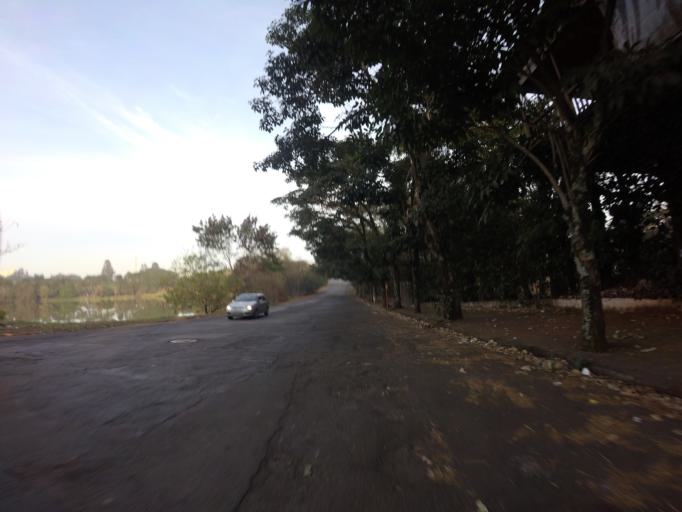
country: BR
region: Sao Paulo
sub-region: Piracicaba
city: Piracicaba
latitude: -22.7333
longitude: -47.5915
